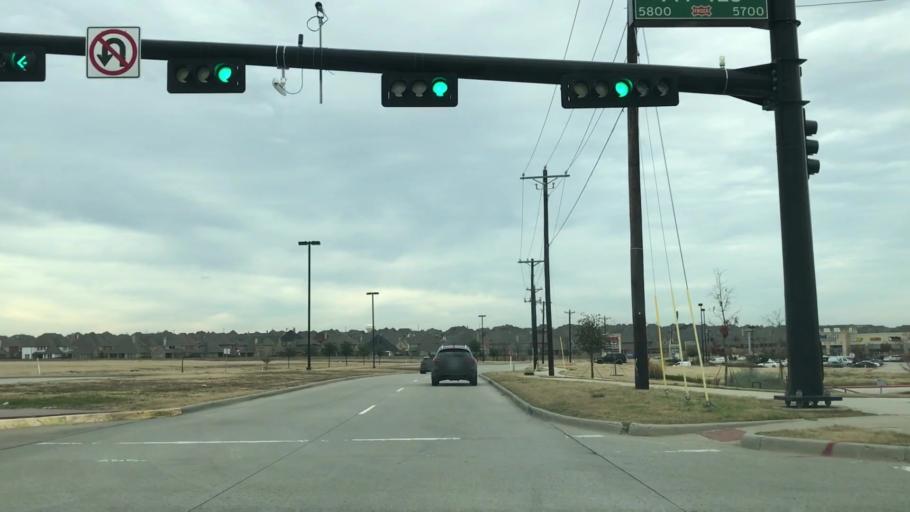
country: US
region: Texas
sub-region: Denton County
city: The Colony
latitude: 33.1272
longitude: -96.8909
